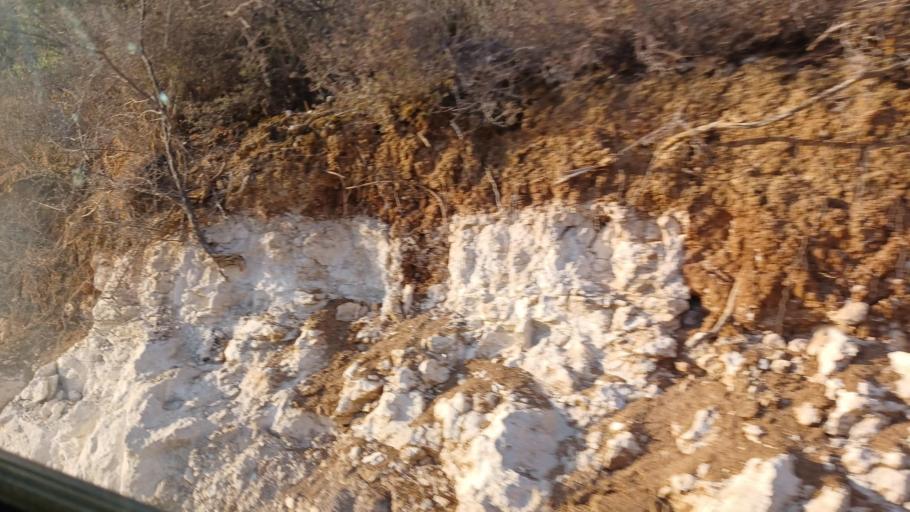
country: CY
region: Pafos
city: Tala
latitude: 34.9221
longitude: 32.5004
